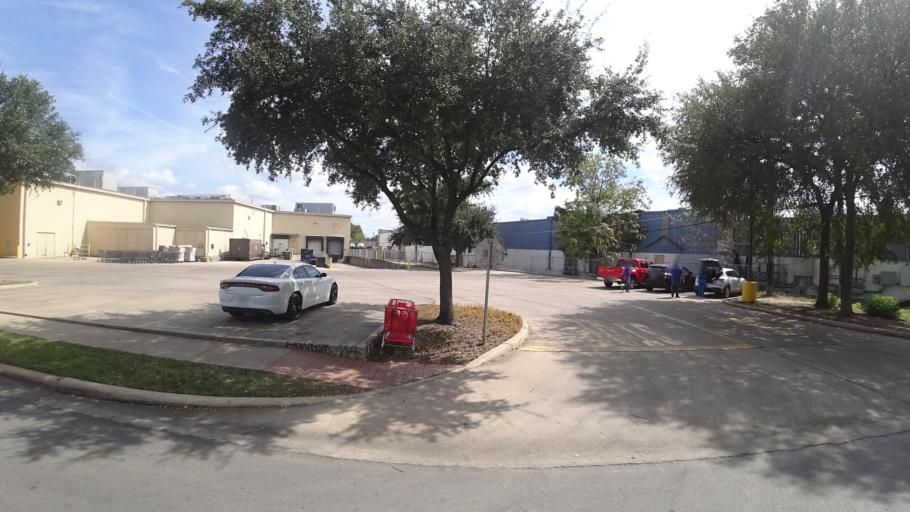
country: US
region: Texas
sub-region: Travis County
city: Austin
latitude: 30.2588
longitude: -97.7124
